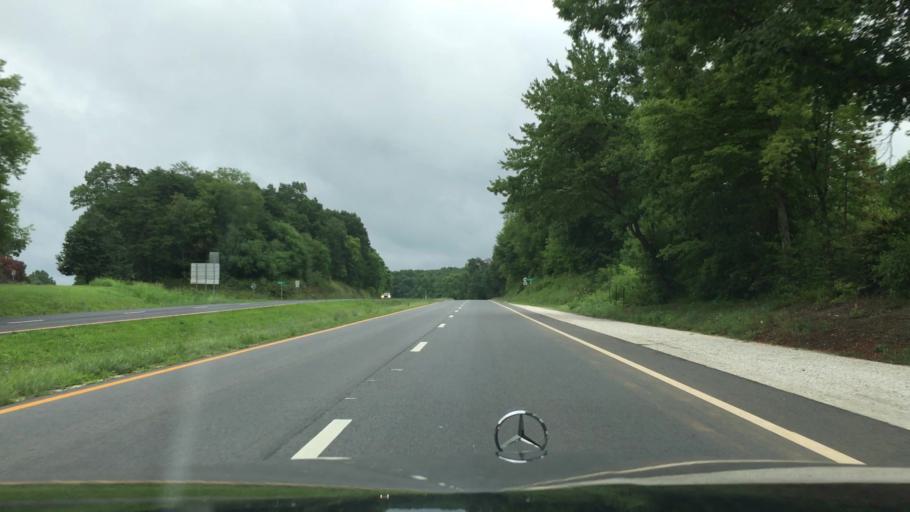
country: US
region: Virginia
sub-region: Campbell County
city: Concord
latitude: 37.3553
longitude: -78.9992
